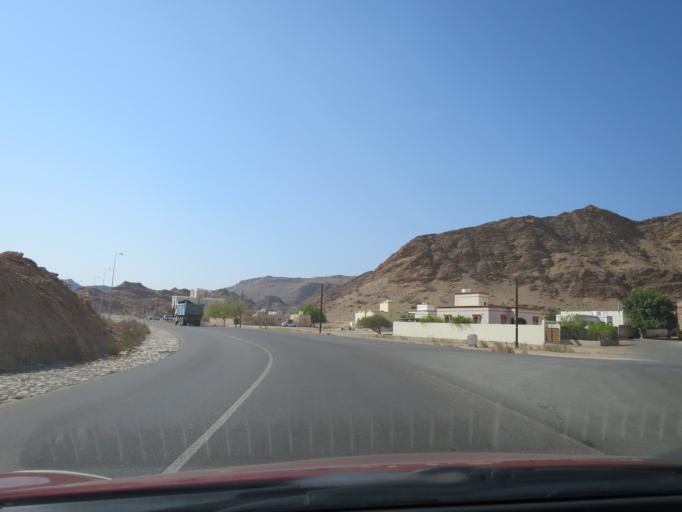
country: OM
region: Muhafazat Masqat
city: Muscat
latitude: 23.5155
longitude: 58.7159
